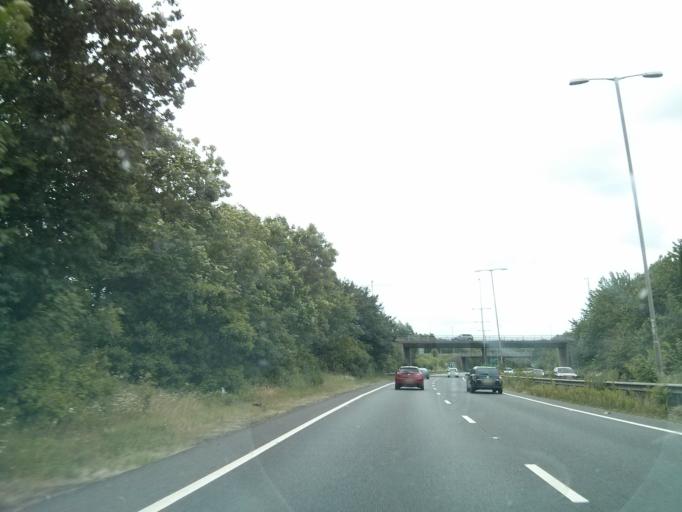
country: GB
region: England
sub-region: Northamptonshire
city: Kettering
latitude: 52.4087
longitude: -0.7553
